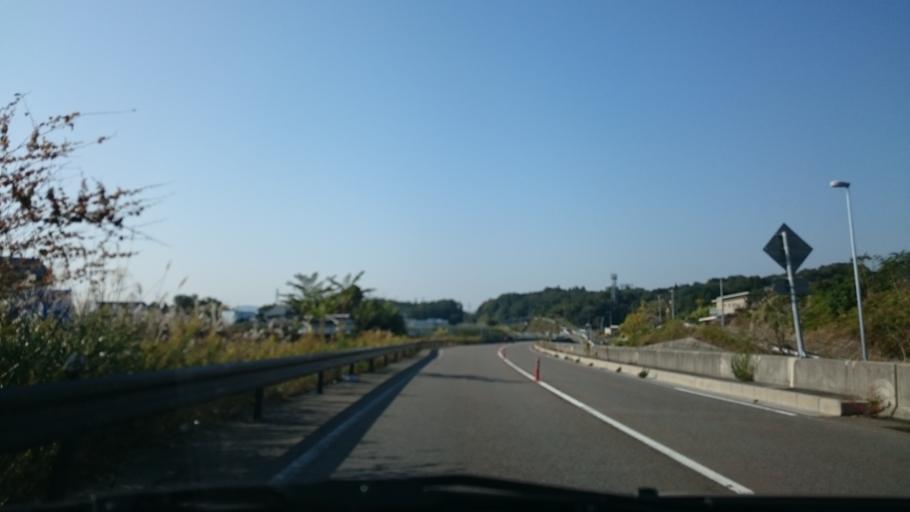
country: JP
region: Gifu
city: Minokamo
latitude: 35.4784
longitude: 137.0451
